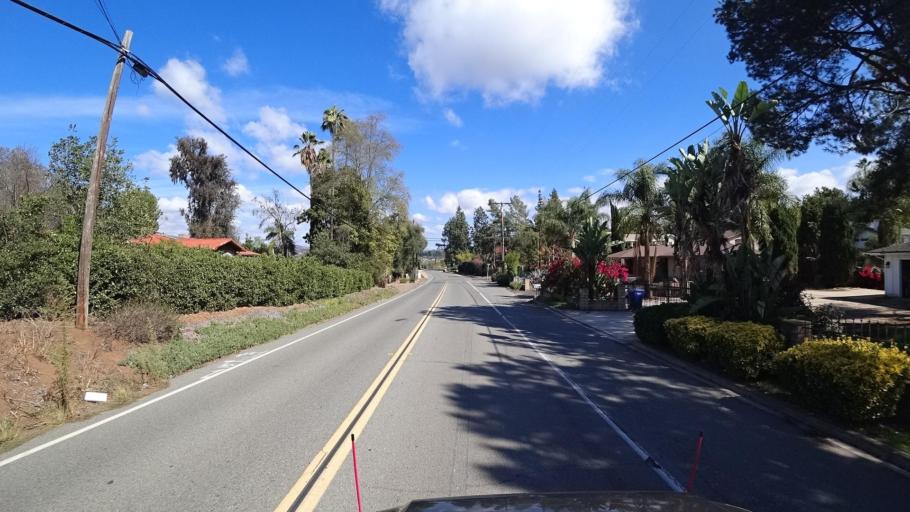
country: US
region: California
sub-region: San Diego County
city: Rancho San Diego
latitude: 32.7696
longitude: -116.9372
